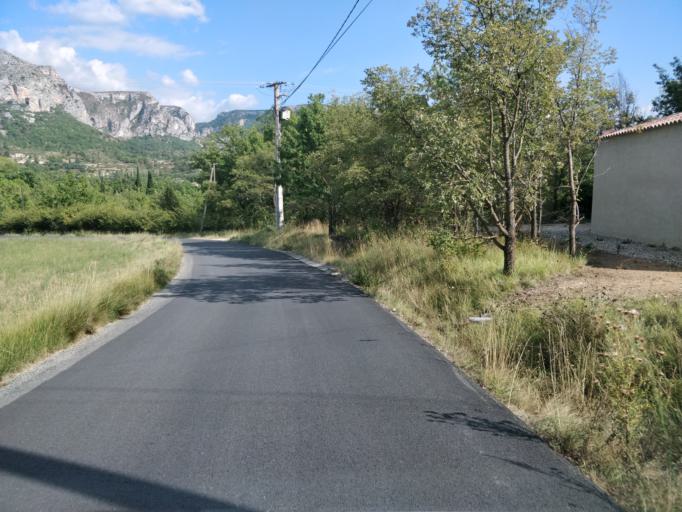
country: FR
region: Provence-Alpes-Cote d'Azur
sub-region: Departement des Alpes-de-Haute-Provence
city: Riez
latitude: 43.8409
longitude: 6.2091
